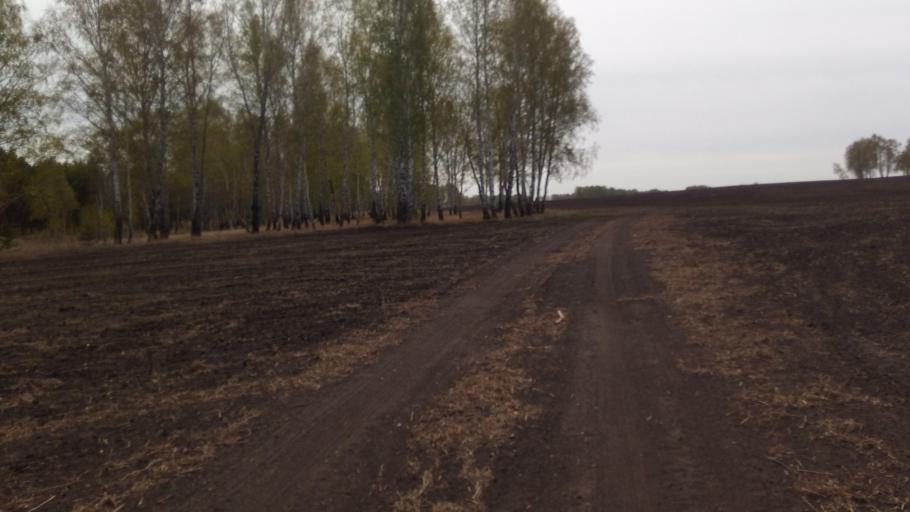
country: RU
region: Chelyabinsk
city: Timiryazevskiy
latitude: 55.0202
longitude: 60.8527
